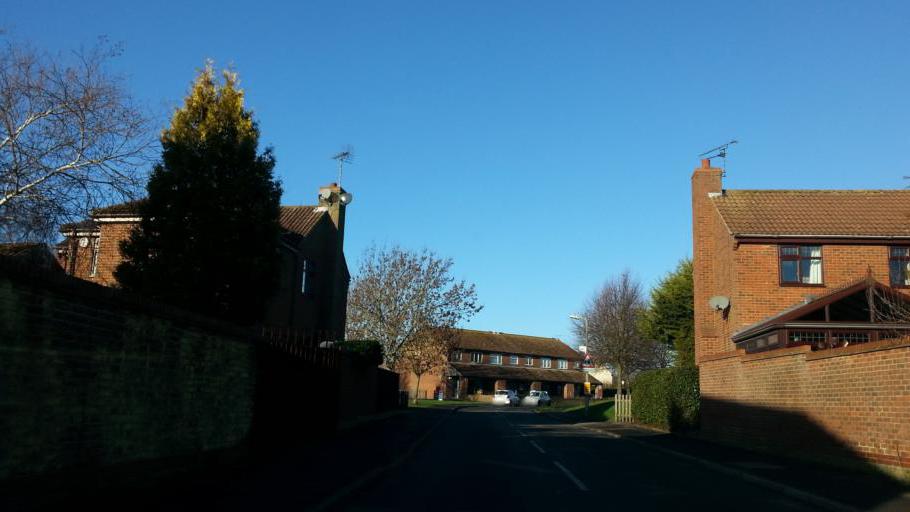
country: GB
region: England
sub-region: Suffolk
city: Felixstowe
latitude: 51.9801
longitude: 1.3236
